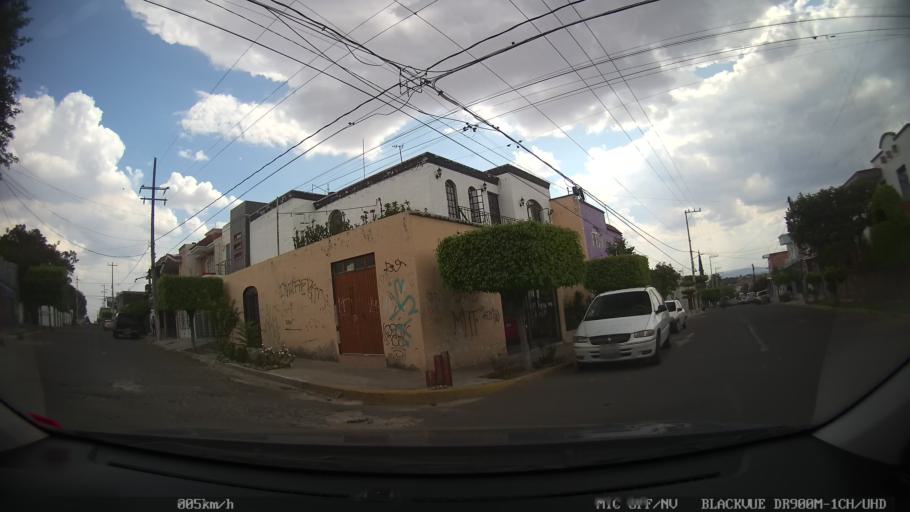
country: MX
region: Jalisco
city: Tlaquepaque
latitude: 20.6328
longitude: -103.2776
